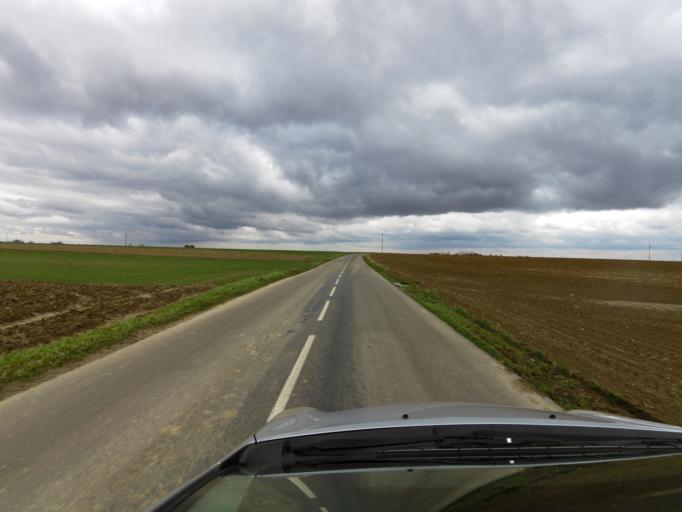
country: FR
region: Picardie
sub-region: Departement de la Somme
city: Roye
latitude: 49.7411
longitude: 2.8021
